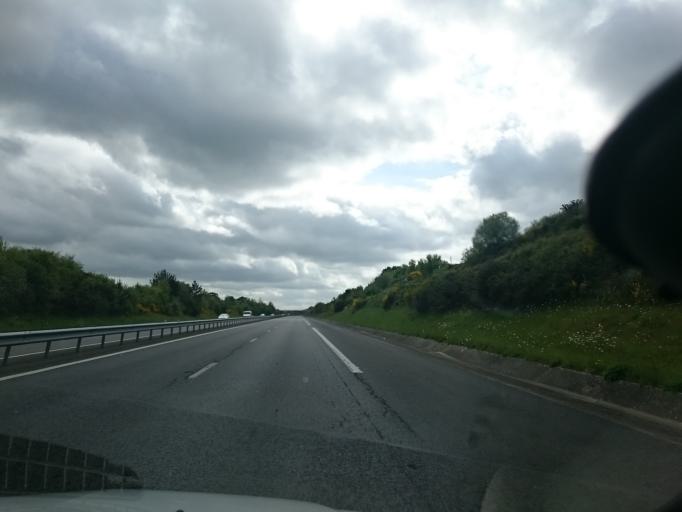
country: FR
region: Brittany
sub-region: Departement d'Ille-et-Vilaine
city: Saint-Jean-sur-Couesnon
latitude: 48.2903
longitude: -1.3774
